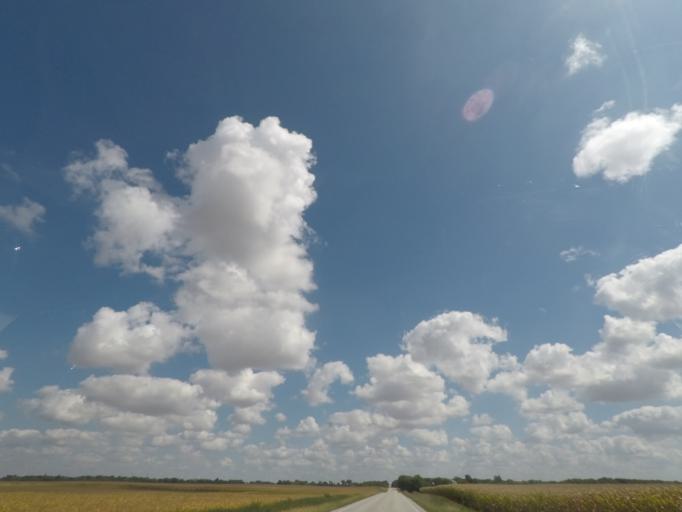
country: US
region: Iowa
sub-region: Story County
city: Nevada
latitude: 42.0778
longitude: -93.3718
